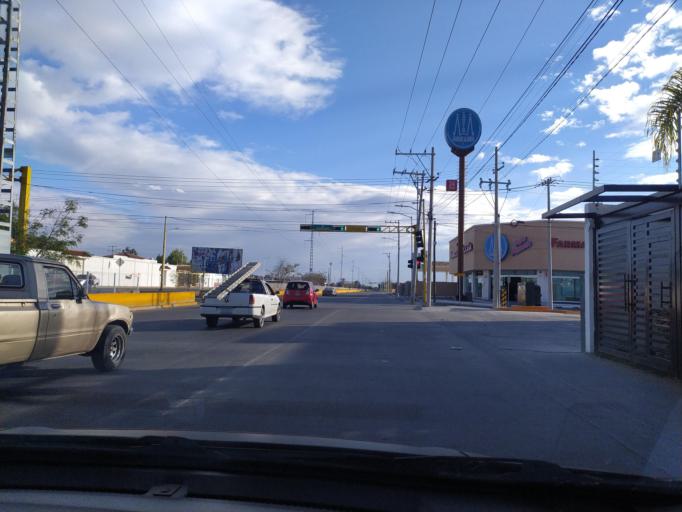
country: MX
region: Guanajuato
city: San Francisco del Rincon
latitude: 21.0173
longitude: -101.8699
